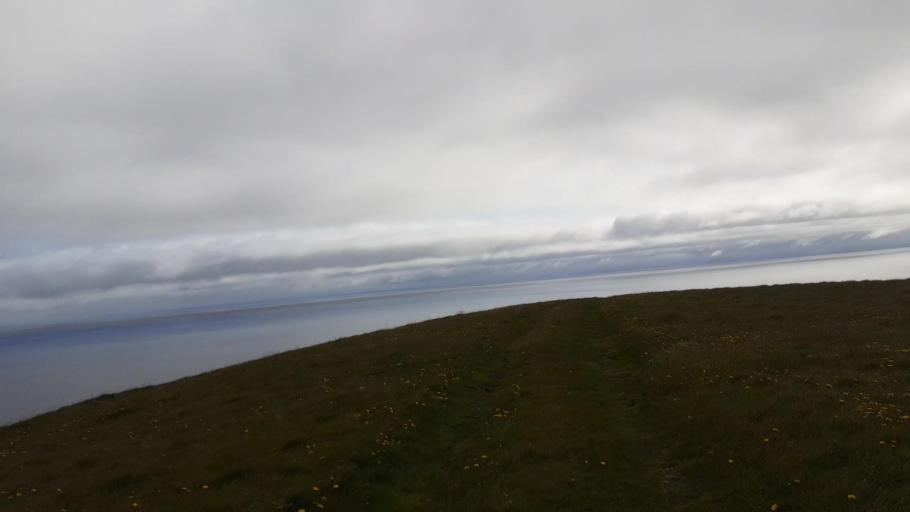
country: IS
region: Northeast
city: Dalvik
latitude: 66.5374
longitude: -17.9816
